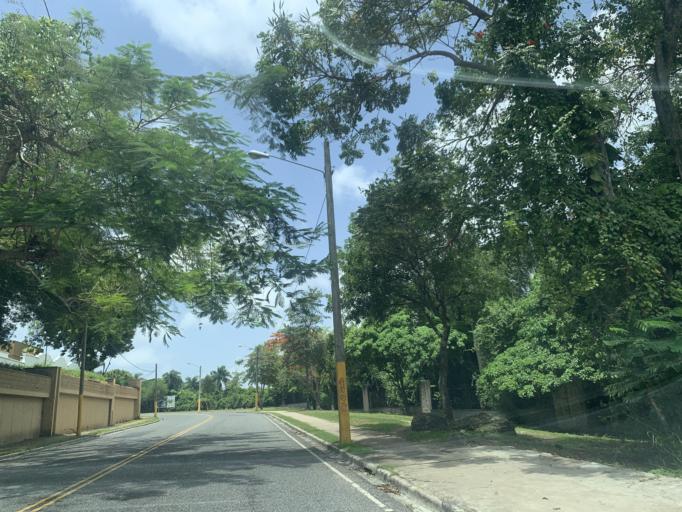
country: DO
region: Nacional
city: La Agustina
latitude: 18.4963
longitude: -69.9487
